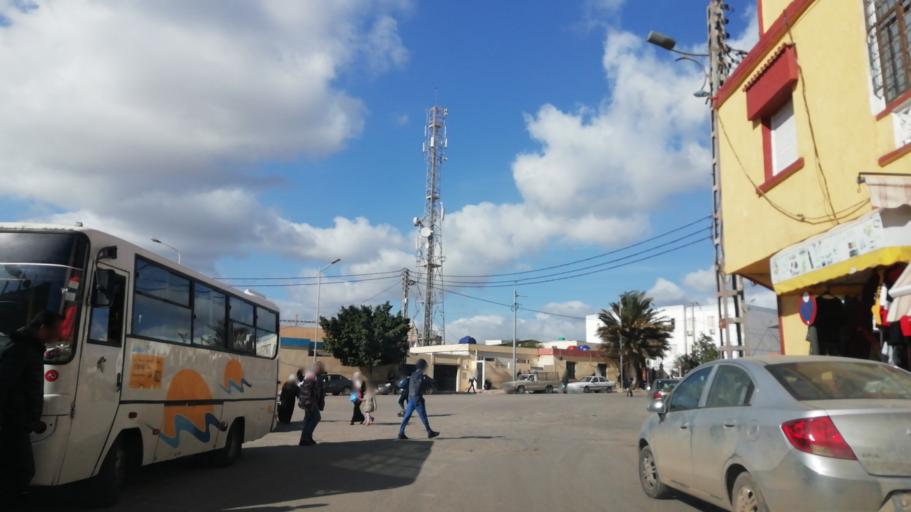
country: DZ
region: Oran
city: Es Senia
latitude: 35.6393
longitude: -0.6670
